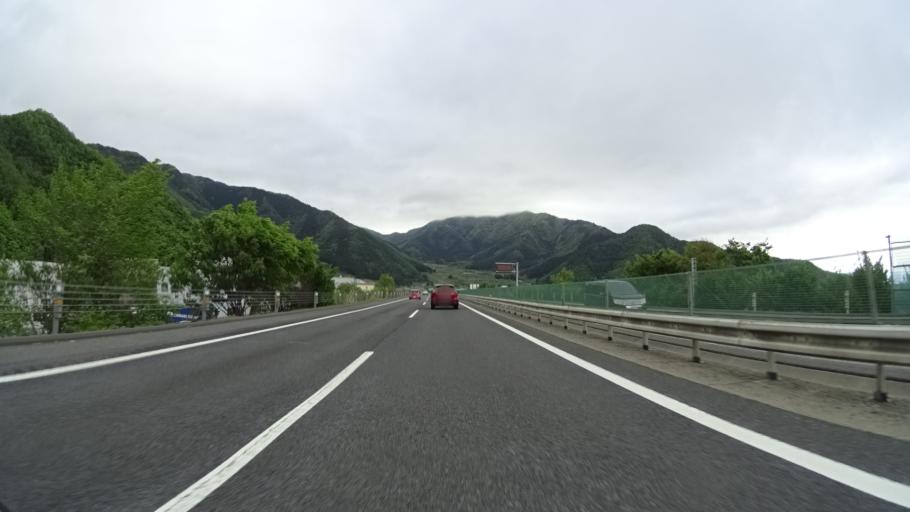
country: JP
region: Nagano
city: Suzaka
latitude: 36.6299
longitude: 138.2732
